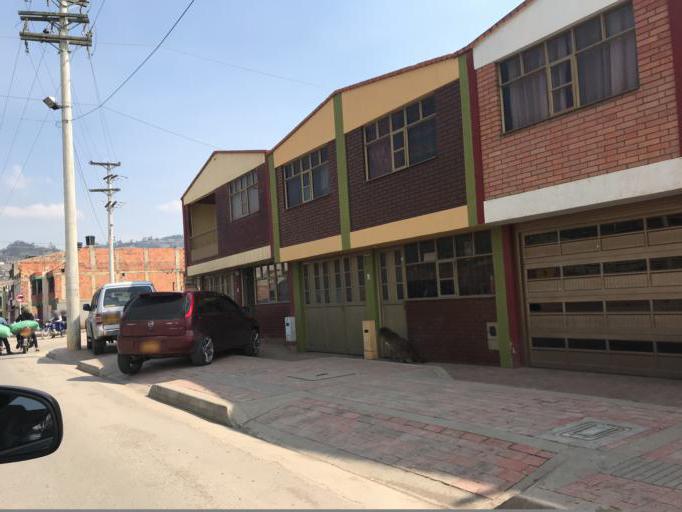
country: CO
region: Boyaca
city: Samaca
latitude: 5.4964
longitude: -73.4884
